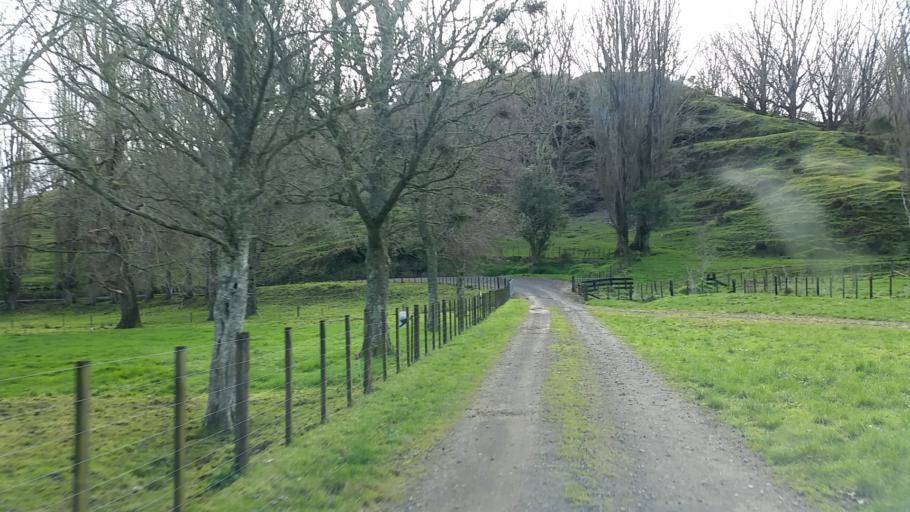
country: NZ
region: Taranaki
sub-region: South Taranaki District
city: Eltham
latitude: -39.2516
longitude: 174.5423
